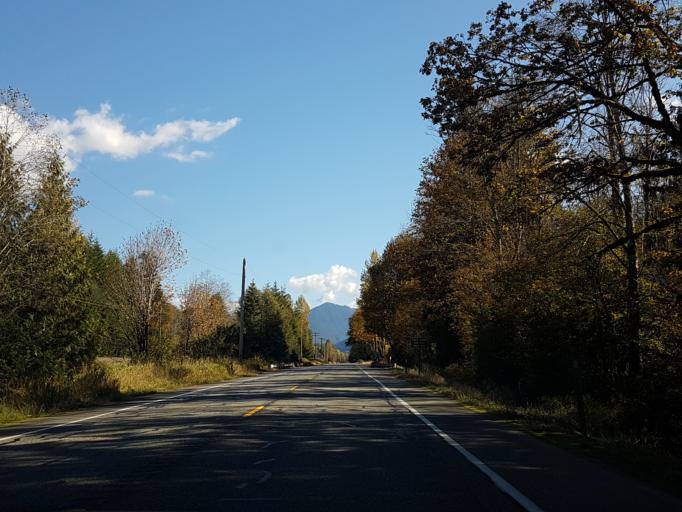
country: US
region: Washington
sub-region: Snohomish County
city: Gold Bar
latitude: 47.7756
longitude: -121.4897
